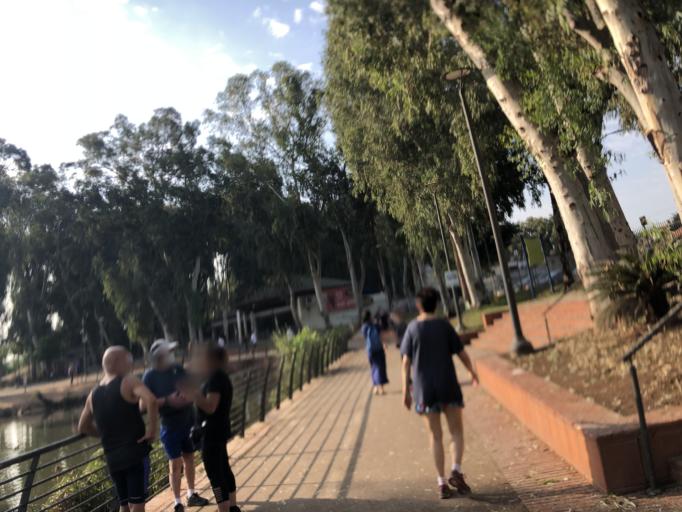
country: IL
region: Tel Aviv
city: Giv`atayim
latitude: 32.0516
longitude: 34.8229
